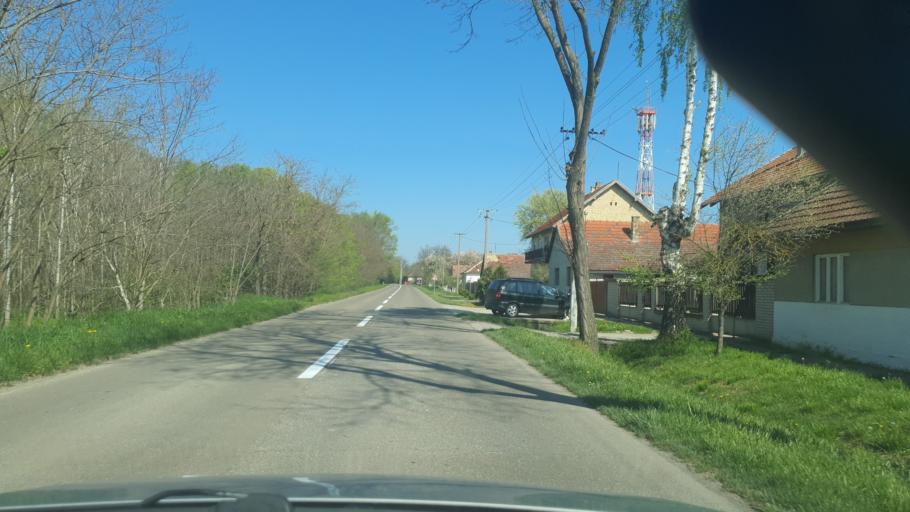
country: RS
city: Kolut
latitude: 45.8822
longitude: 18.9329
